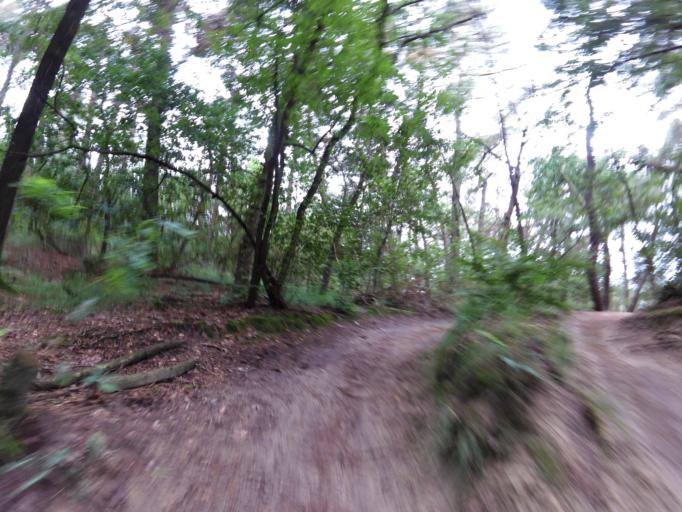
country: NL
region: North Brabant
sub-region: Gemeente Loon op Zand
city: Loon op Zand
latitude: 51.6551
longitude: 5.1323
